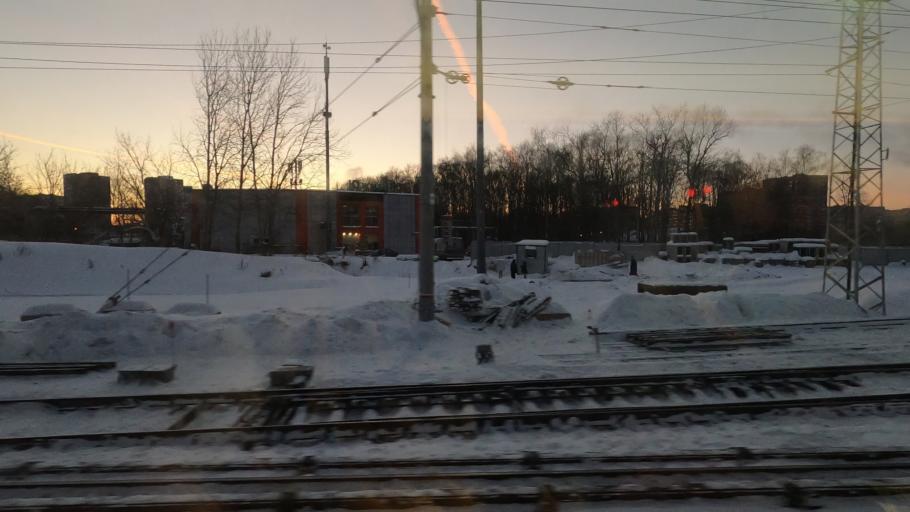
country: RU
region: Moskovskaya
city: Lobnya
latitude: 56.0089
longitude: 37.4870
